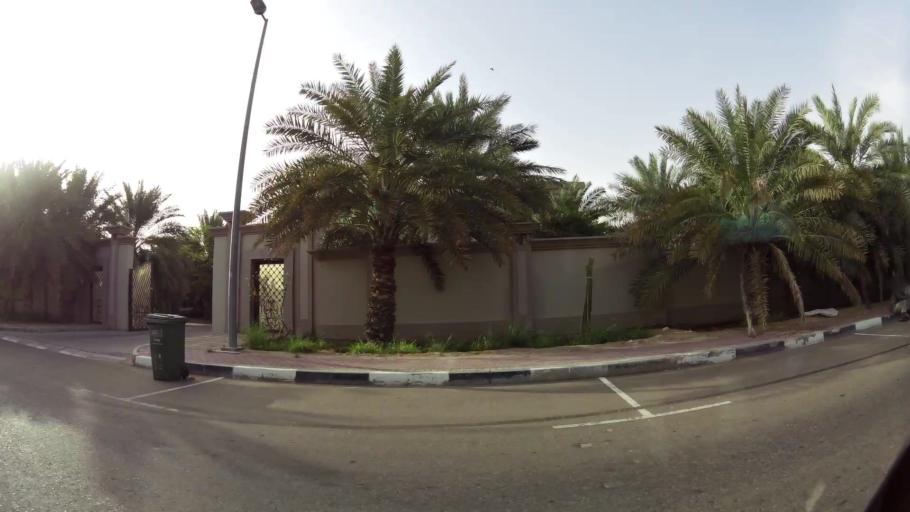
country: AE
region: Abu Dhabi
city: Al Ain
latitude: 24.1272
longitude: 55.6954
